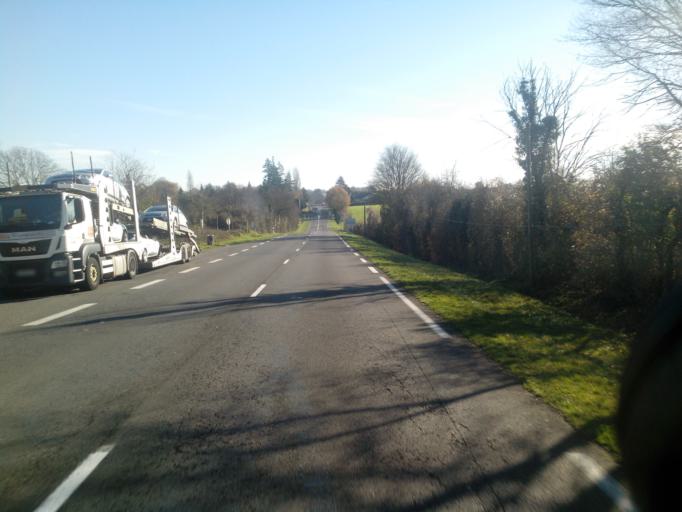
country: FR
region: Poitou-Charentes
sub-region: Departement de la Vienne
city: Terce
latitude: 46.4396
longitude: 0.5878
